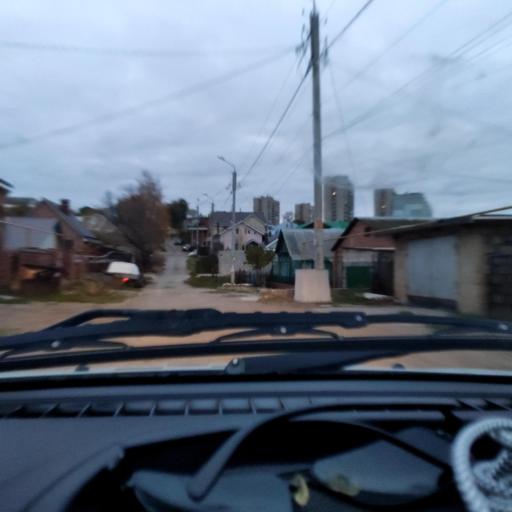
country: RU
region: Samara
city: Zhigulevsk
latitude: 53.4855
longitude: 49.5220
